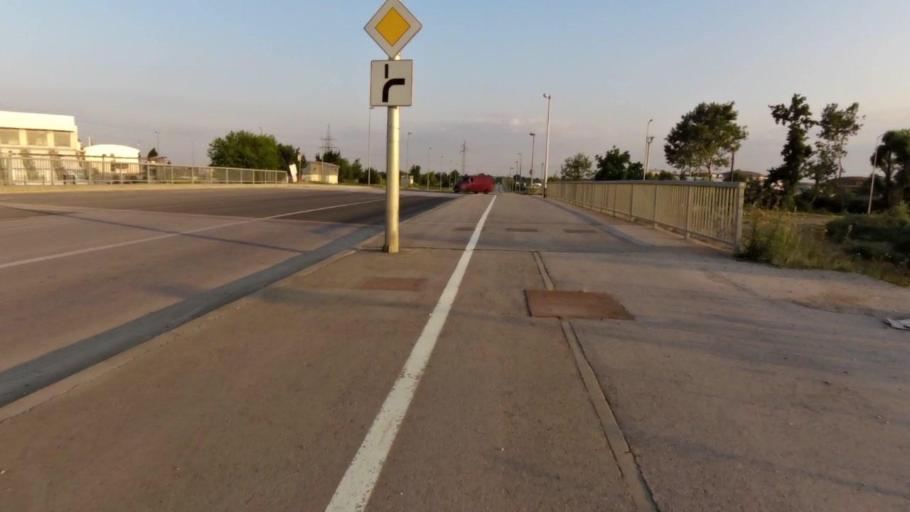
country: HR
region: Grad Zagreb
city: Dubrava
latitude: 45.7937
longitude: 16.0790
